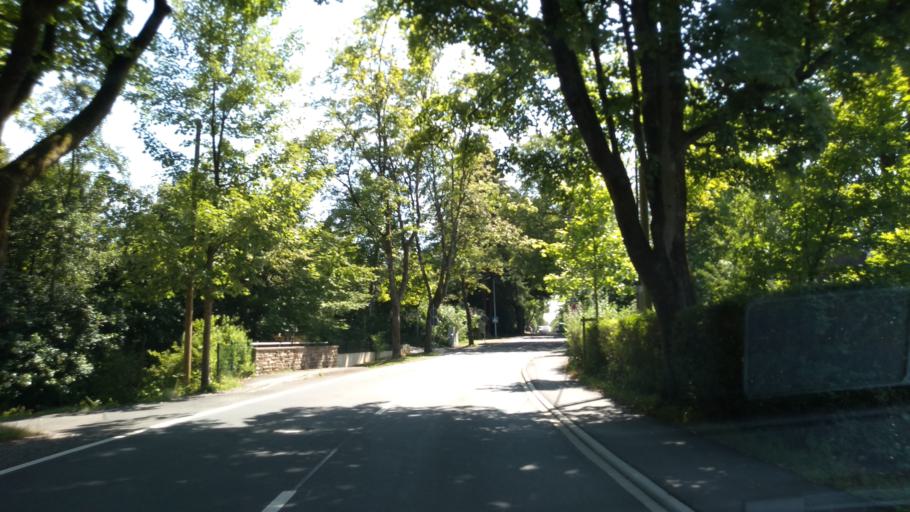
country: DE
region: North Rhine-Westphalia
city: Kreuztal
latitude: 50.9737
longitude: 7.9796
